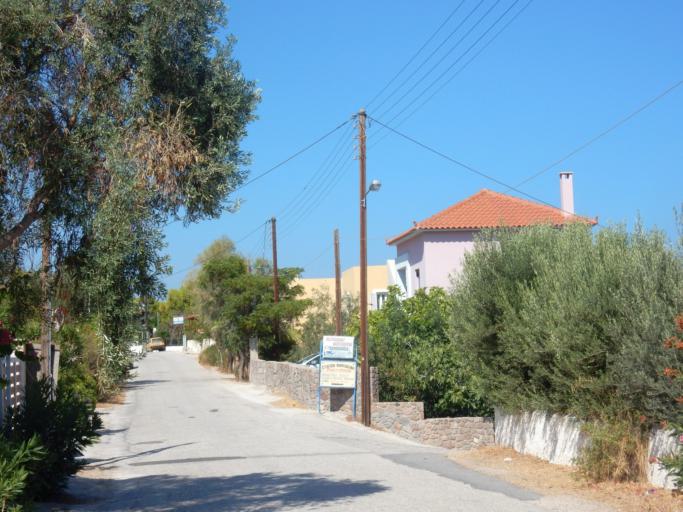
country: GR
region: Attica
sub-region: Nomos Piraios
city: Vathi
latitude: 37.7711
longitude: 23.5297
